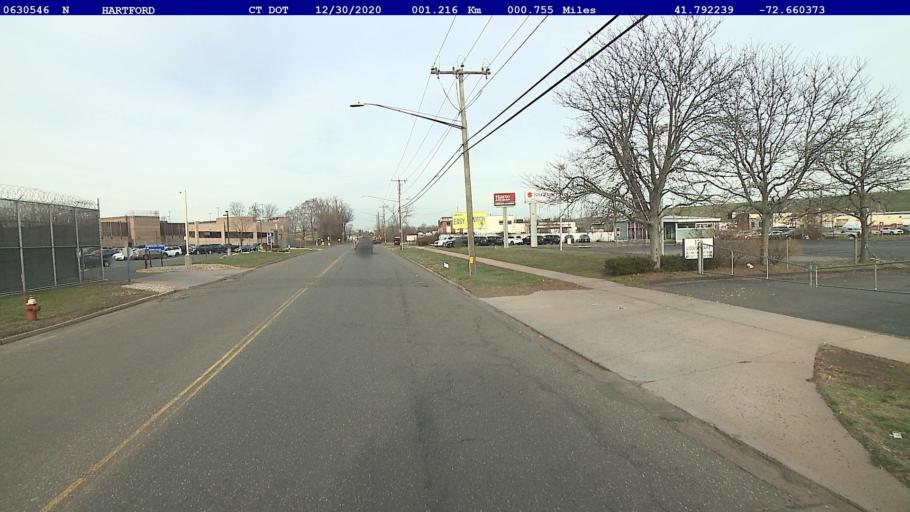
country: US
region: Connecticut
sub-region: Hartford County
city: Hartford
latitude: 41.7922
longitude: -72.6604
